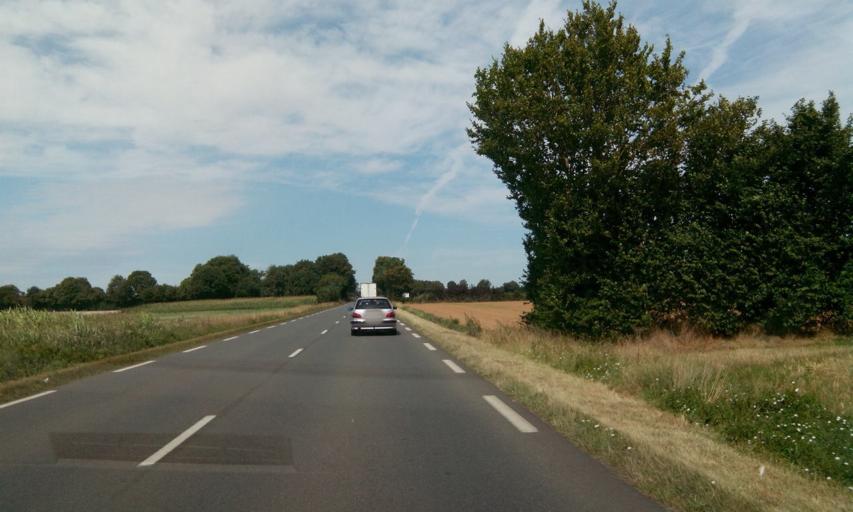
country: FR
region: Poitou-Charentes
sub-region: Departement des Deux-Sevres
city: Lezay
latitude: 46.1696
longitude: 0.0073
